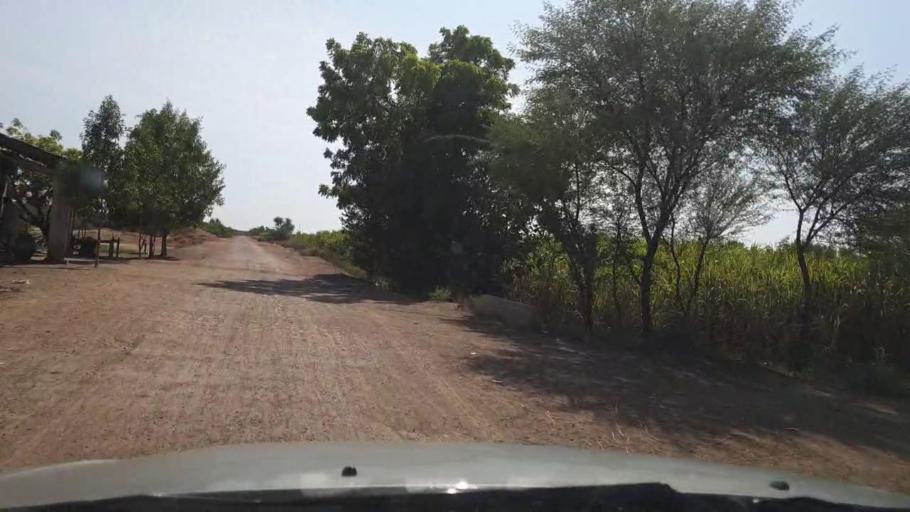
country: PK
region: Sindh
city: Bulri
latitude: 25.0071
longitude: 68.3203
